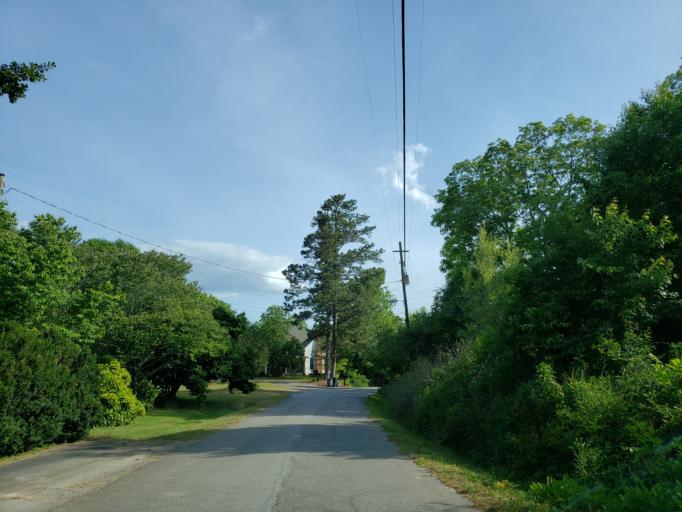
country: US
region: Georgia
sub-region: Carroll County
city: Carrollton
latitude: 33.4521
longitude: -85.1319
